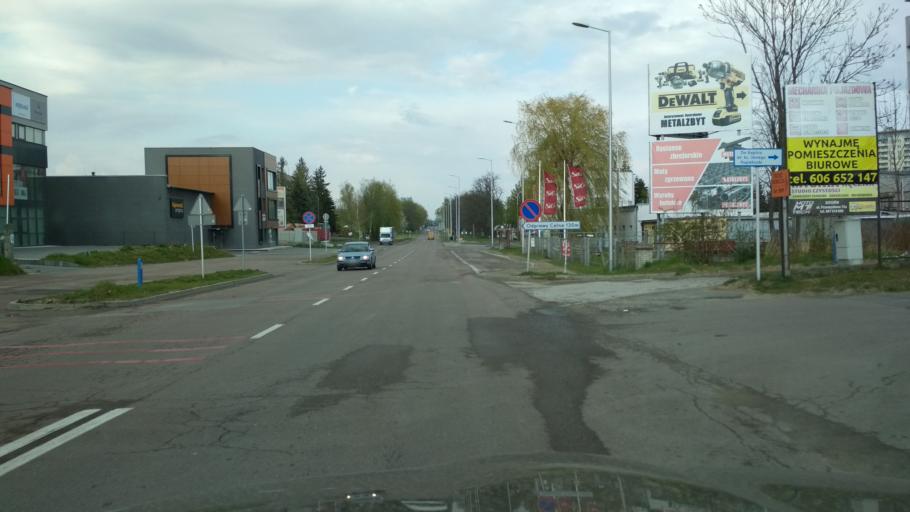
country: PL
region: Subcarpathian Voivodeship
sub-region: Powiat rzeszowski
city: Kielanowka
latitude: 50.0186
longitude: 21.9650
